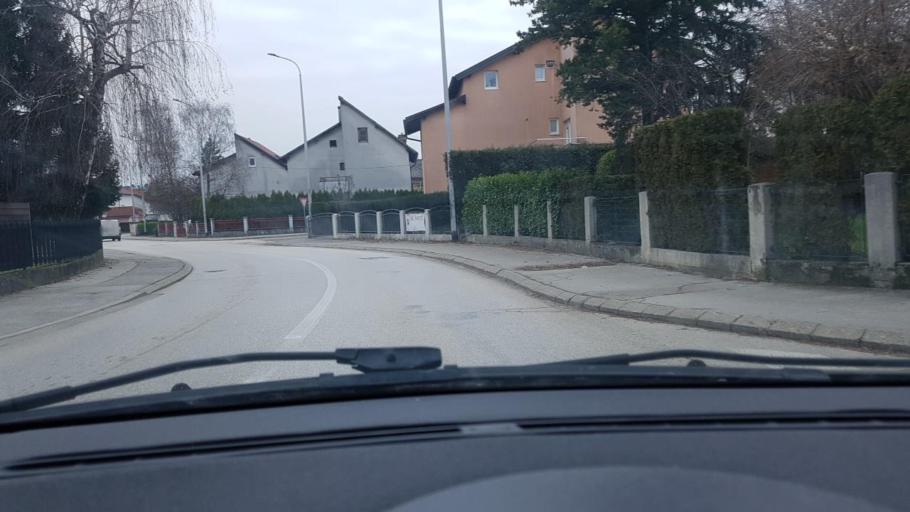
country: HR
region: Zagrebacka
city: Brdovec
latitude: 45.8652
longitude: 15.7964
